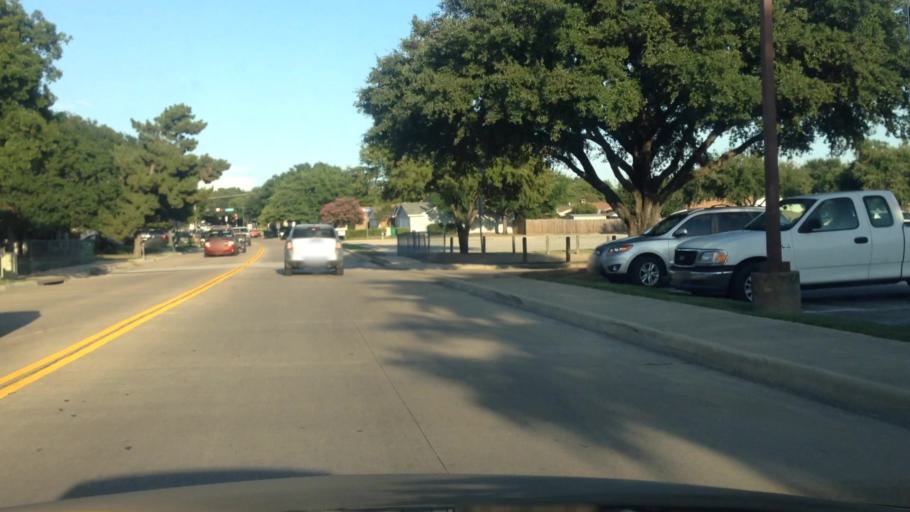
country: US
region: Texas
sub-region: Tarrant County
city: Watauga
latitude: 32.8815
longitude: -97.2410
